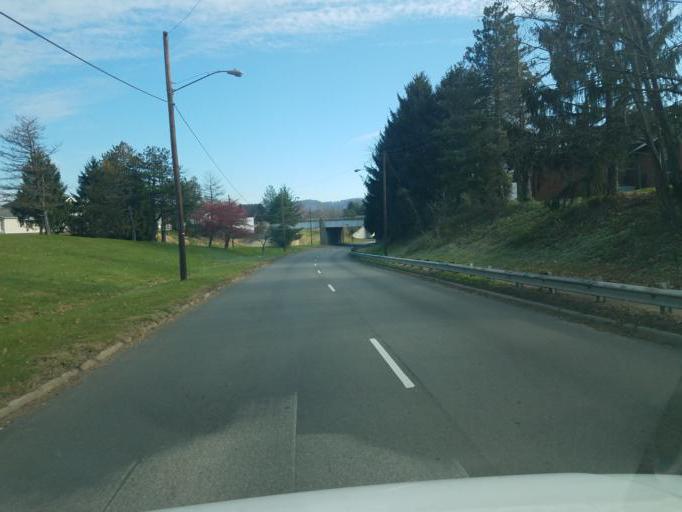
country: US
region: Ohio
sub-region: Scioto County
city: Portsmouth
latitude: 38.7395
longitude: -82.9917
